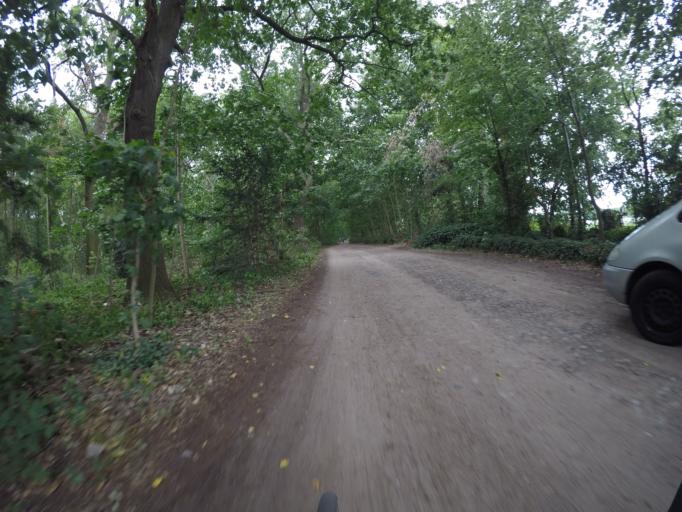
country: DE
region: Berlin
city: Siemensstadt
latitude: 52.5725
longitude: 13.2587
